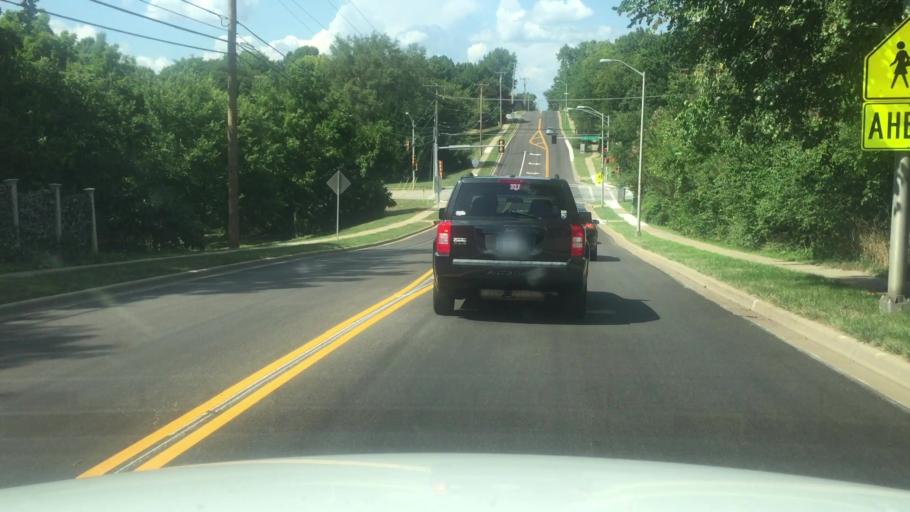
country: US
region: Kansas
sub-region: Johnson County
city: Lenexa
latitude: 38.9774
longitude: -94.7423
